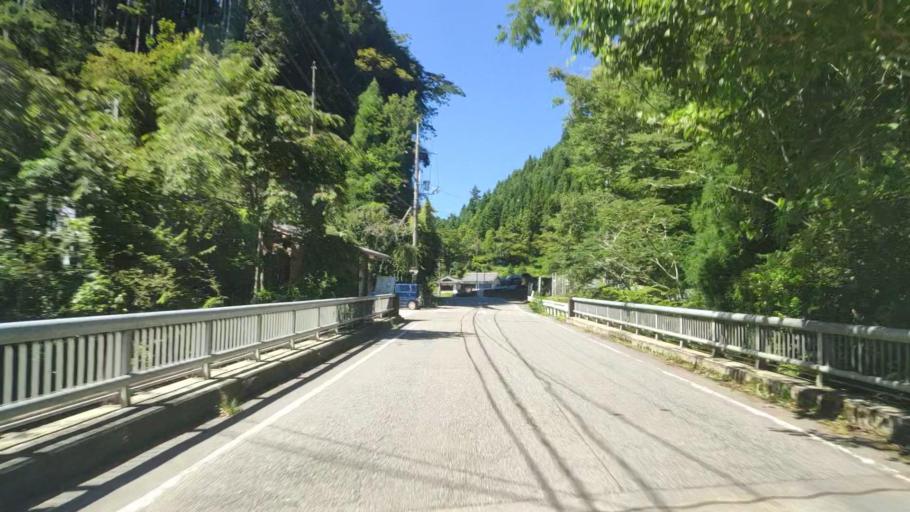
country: JP
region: Nara
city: Yoshino-cho
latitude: 34.4137
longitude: 135.9345
